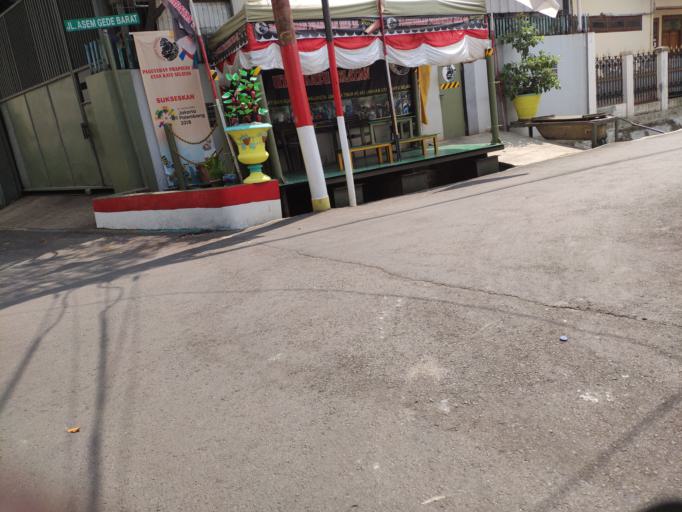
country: ID
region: Jakarta Raya
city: Jakarta
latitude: -6.2017
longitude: 106.8695
